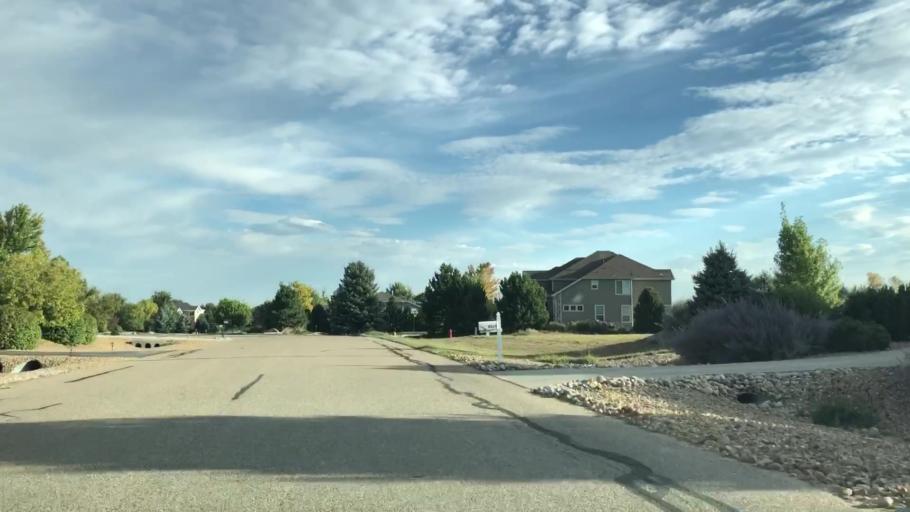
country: US
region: Colorado
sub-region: Weld County
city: Windsor
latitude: 40.4387
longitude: -104.9616
